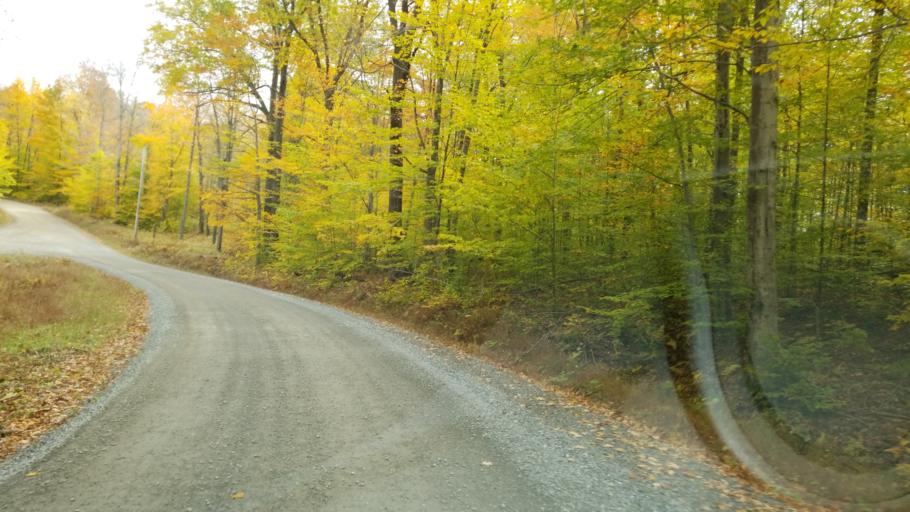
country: US
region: Pennsylvania
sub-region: Clearfield County
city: Clearfield
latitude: 41.1928
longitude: -78.3852
